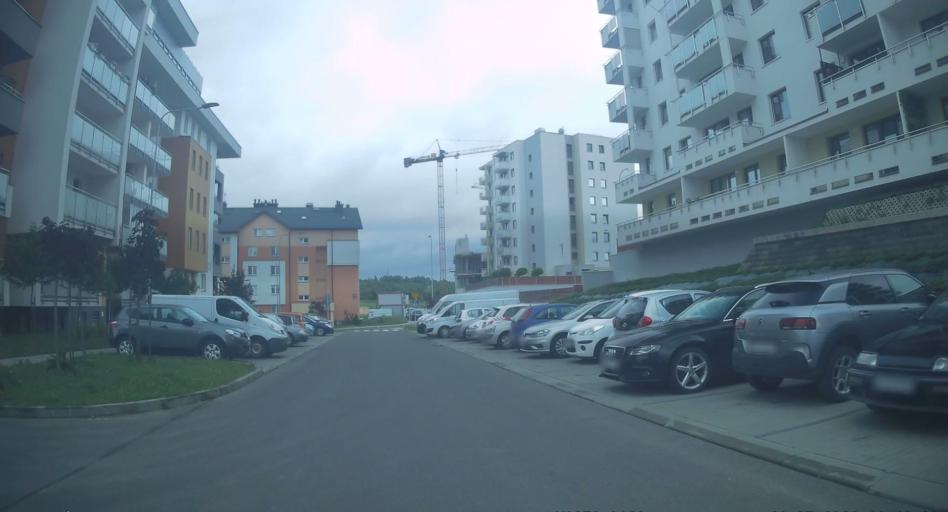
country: PL
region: Subcarpathian Voivodeship
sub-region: Rzeszow
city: Przybyszowka
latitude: 50.0462
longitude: 21.9482
